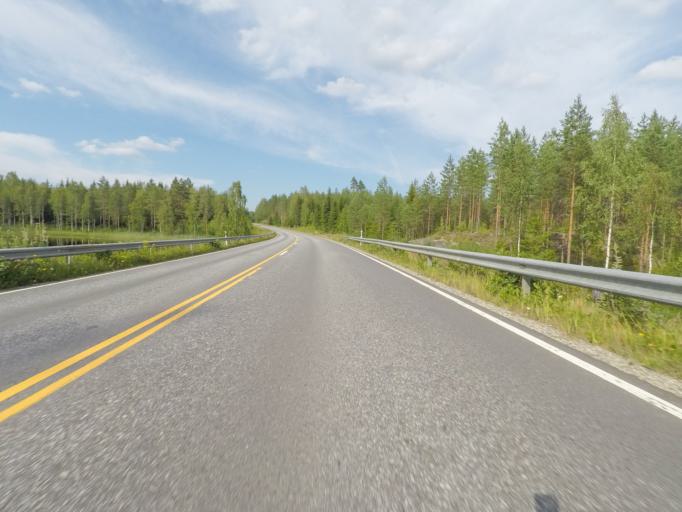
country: FI
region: Southern Savonia
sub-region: Savonlinna
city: Sulkava
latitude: 61.8938
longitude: 28.5760
